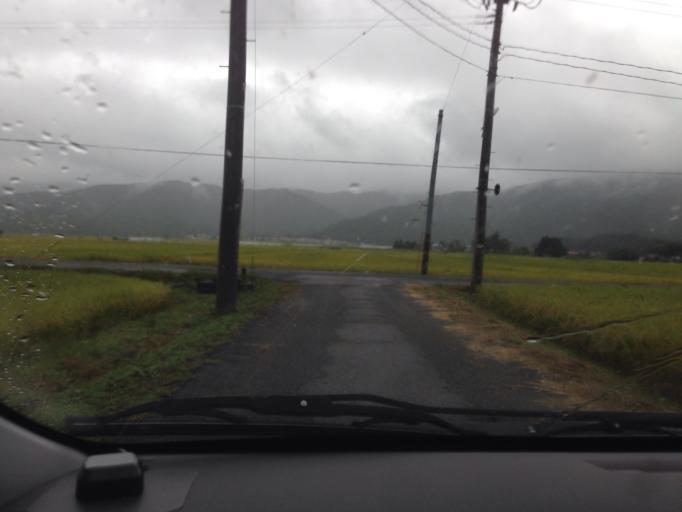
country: JP
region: Fukushima
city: Inawashiro
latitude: 37.4142
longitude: 140.1253
